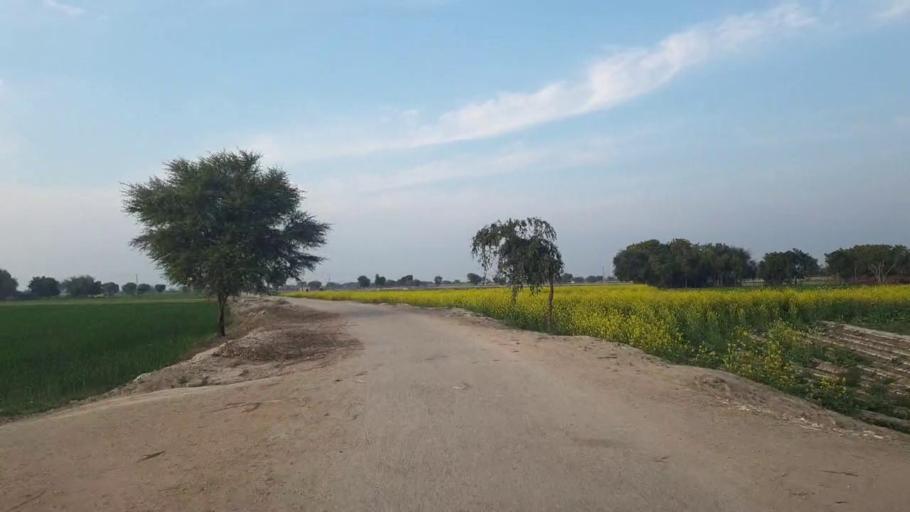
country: PK
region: Sindh
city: Shahpur Chakar
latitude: 26.0992
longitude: 68.5485
